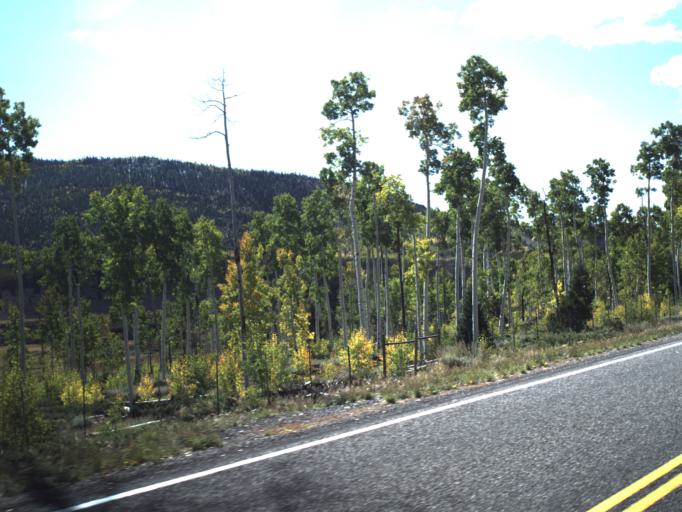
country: US
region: Utah
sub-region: Wayne County
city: Loa
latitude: 38.5260
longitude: -111.7483
